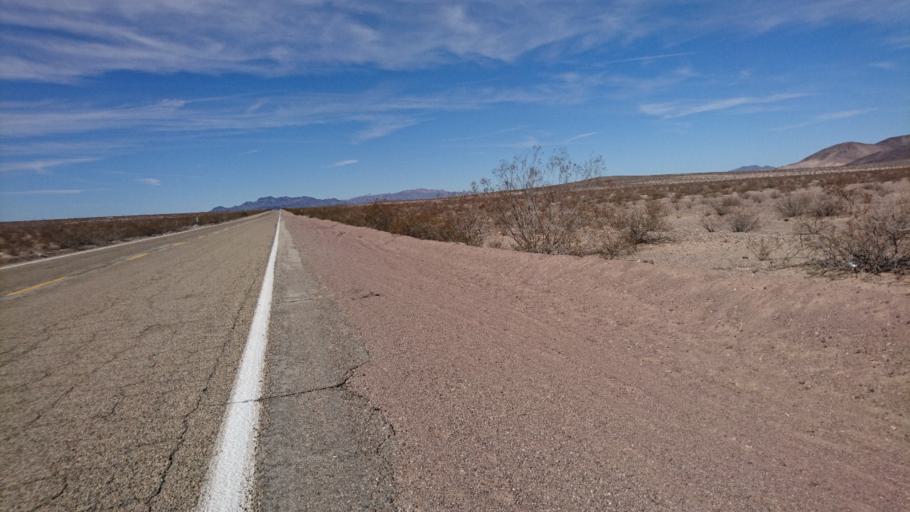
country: US
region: California
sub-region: San Bernardino County
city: Twentynine Palms
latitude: 34.7032
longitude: -116.0711
